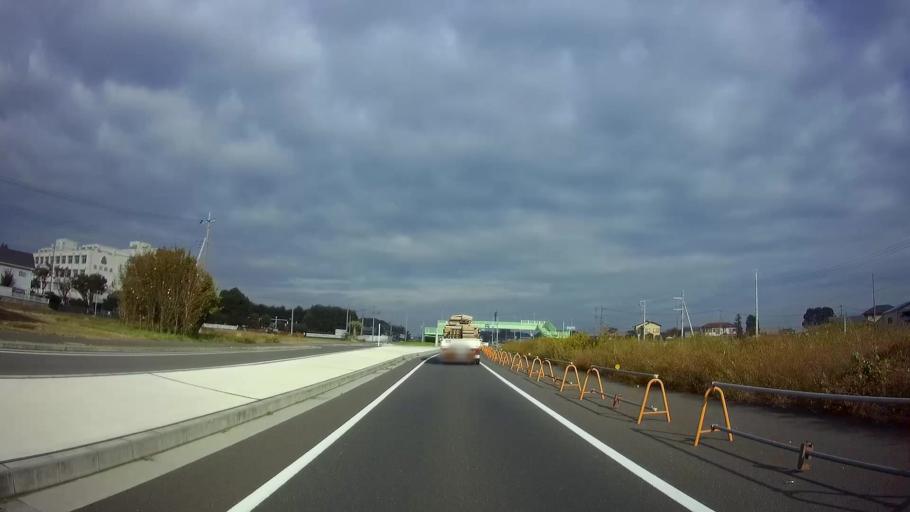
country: JP
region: Saitama
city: Okegawa
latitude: 35.9837
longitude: 139.5335
